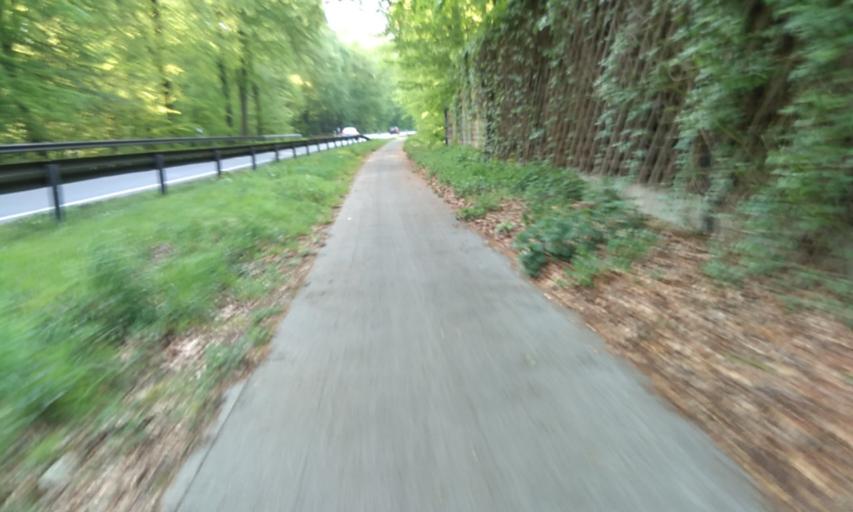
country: DE
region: Lower Saxony
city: Buxtehude
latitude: 53.4741
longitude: 9.6519
